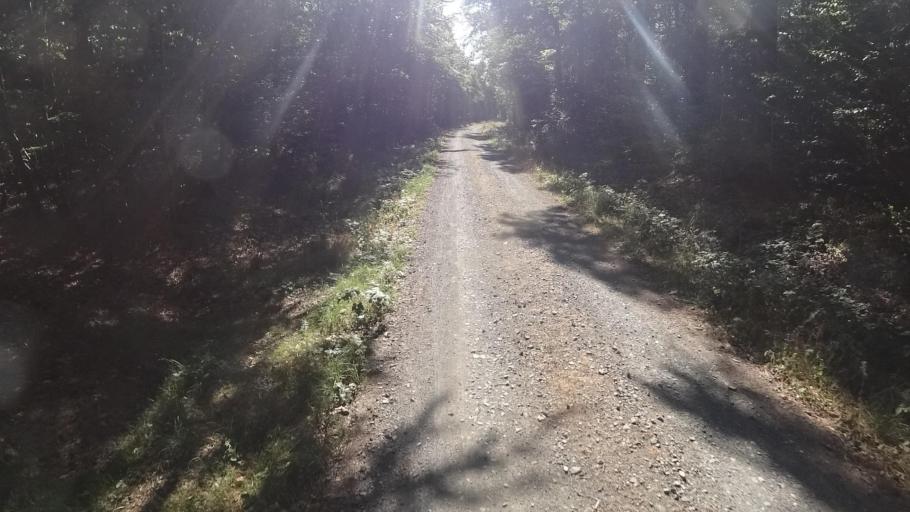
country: DE
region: Rheinland-Pfalz
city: Reich
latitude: 49.9908
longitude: 7.4283
